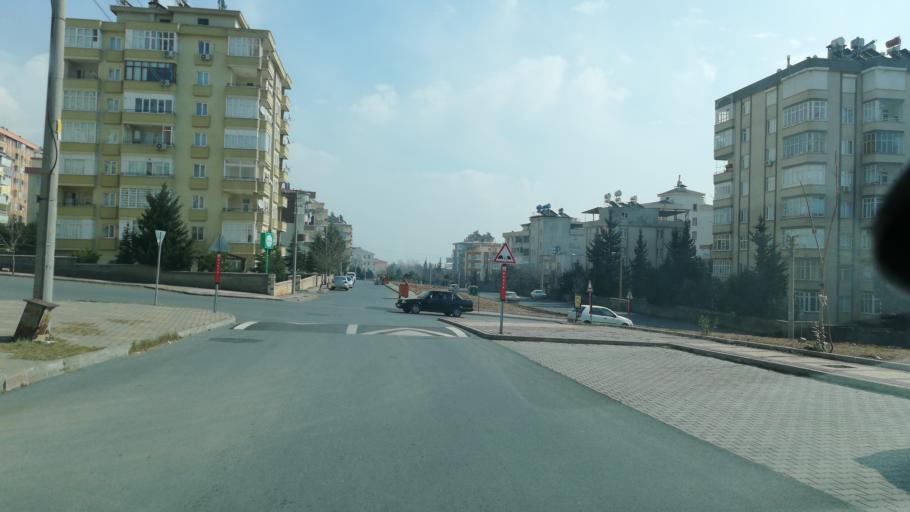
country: TR
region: Kahramanmaras
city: Kahramanmaras
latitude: 37.5890
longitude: 36.8965
